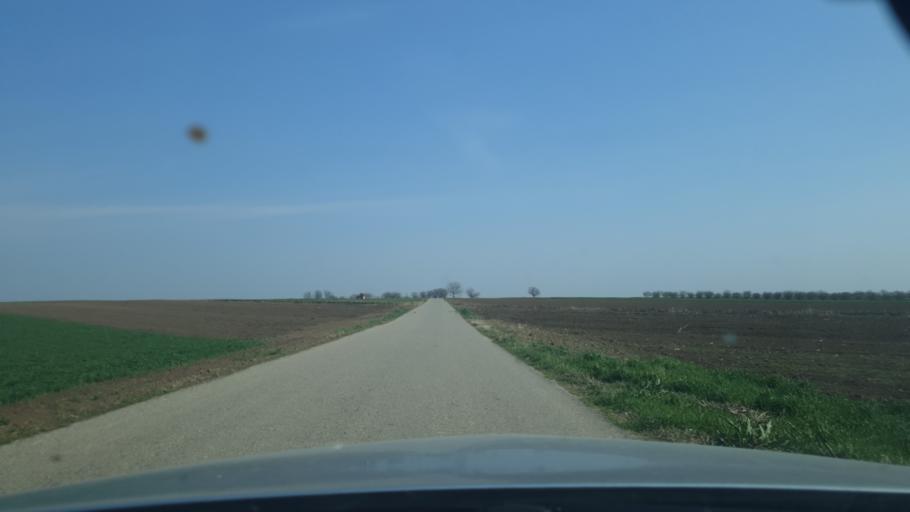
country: RS
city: Putinci
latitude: 45.0547
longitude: 19.9317
